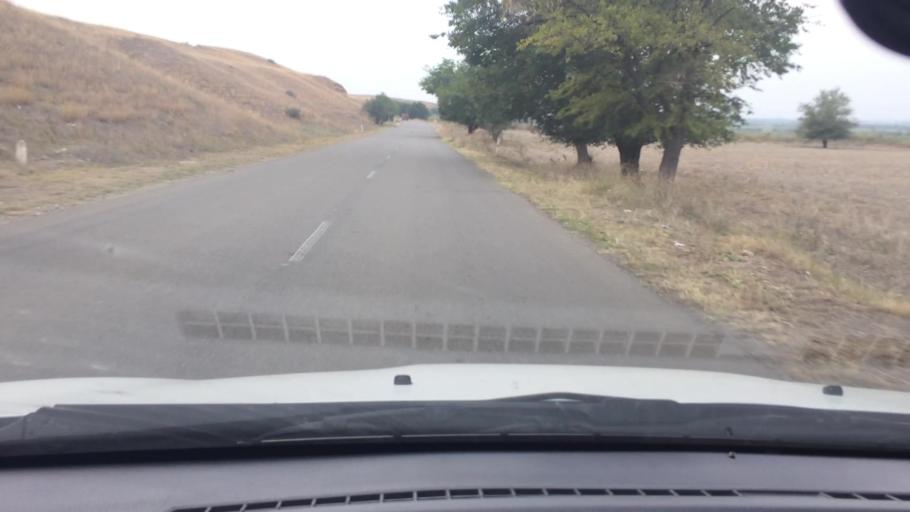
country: AM
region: Tavush
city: Berdavan
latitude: 41.3382
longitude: 45.0055
